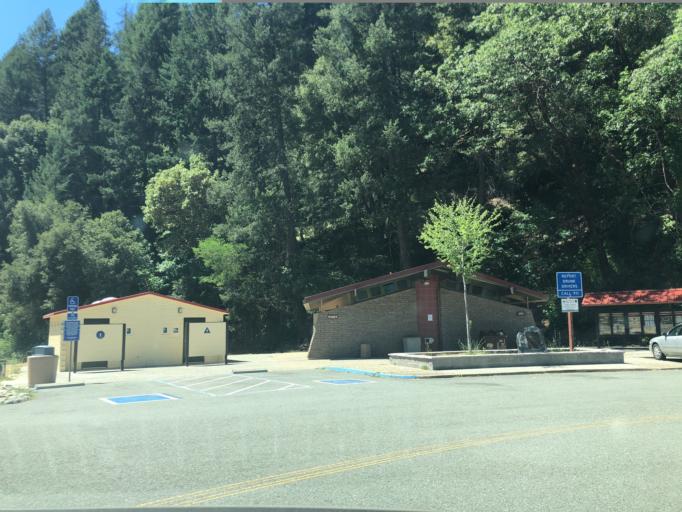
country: US
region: California
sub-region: Trinity County
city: Weaverville
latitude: 40.6662
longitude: -122.9432
